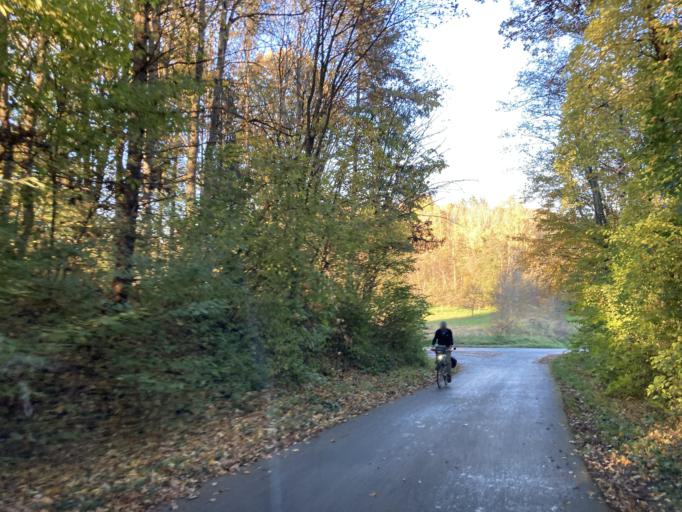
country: DE
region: Baden-Wuerttemberg
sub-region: Tuebingen Region
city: Hirrlingen
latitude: 48.4336
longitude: 8.9195
